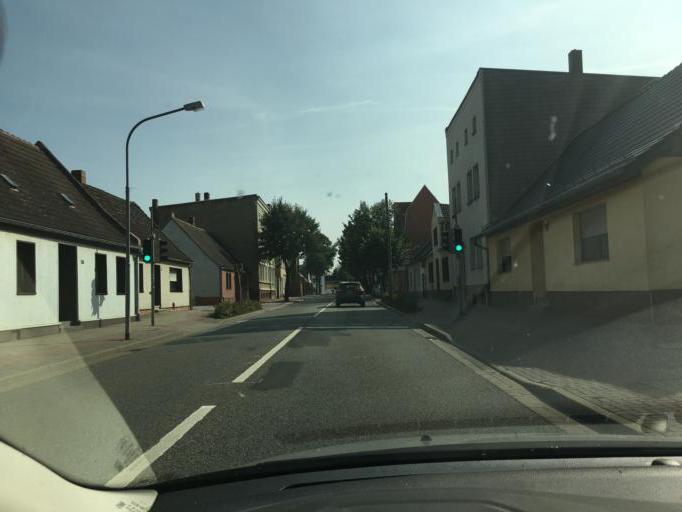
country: DE
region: Saxony-Anhalt
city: Calbe
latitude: 51.8991
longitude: 11.7712
